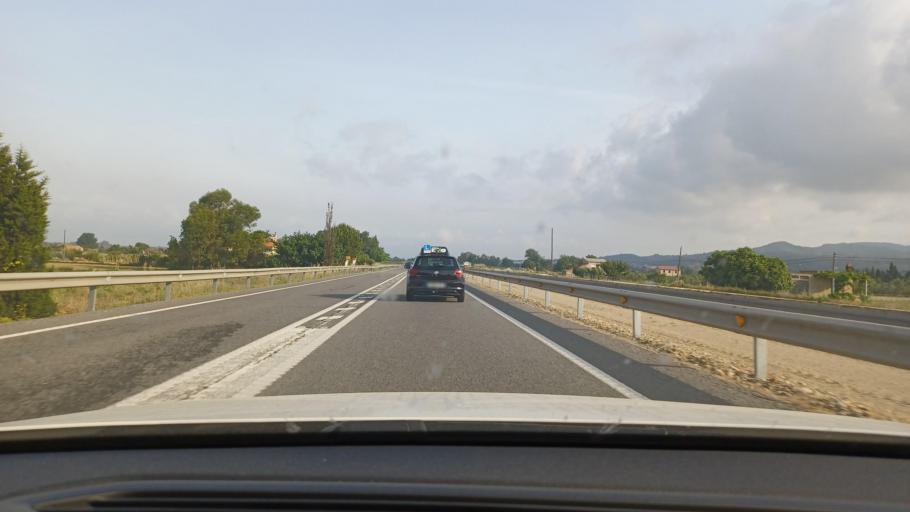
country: ES
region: Catalonia
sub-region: Provincia de Tarragona
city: Amposta
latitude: 40.7444
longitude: 0.5615
